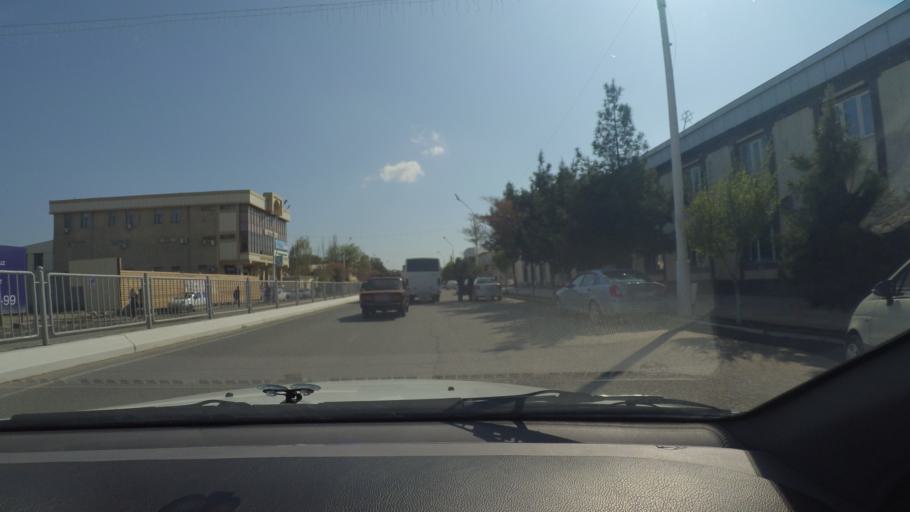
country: UZ
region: Bukhara
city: Bukhara
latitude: 39.7660
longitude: 64.4306
